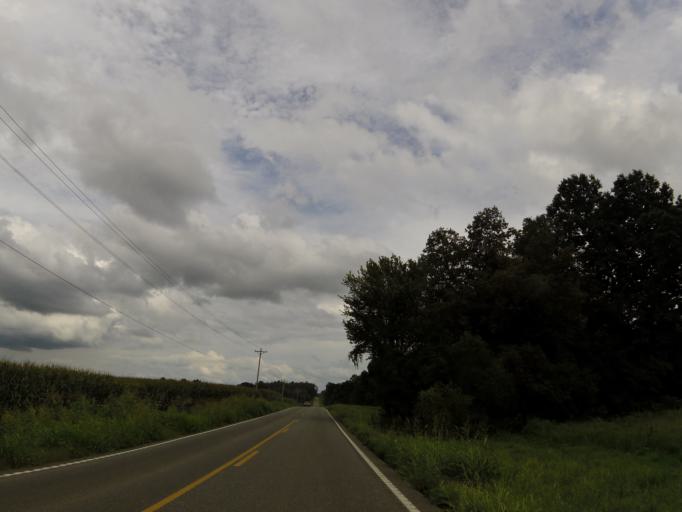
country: US
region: Kentucky
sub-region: Ballard County
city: La Center
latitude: 36.9909
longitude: -88.9068
